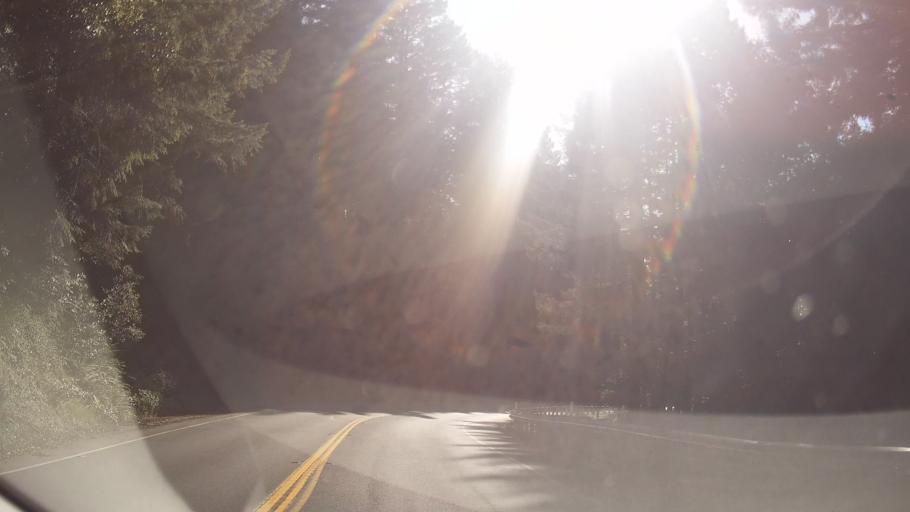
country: US
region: California
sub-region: Mendocino County
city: Brooktrails
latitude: 39.3973
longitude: -123.4518
